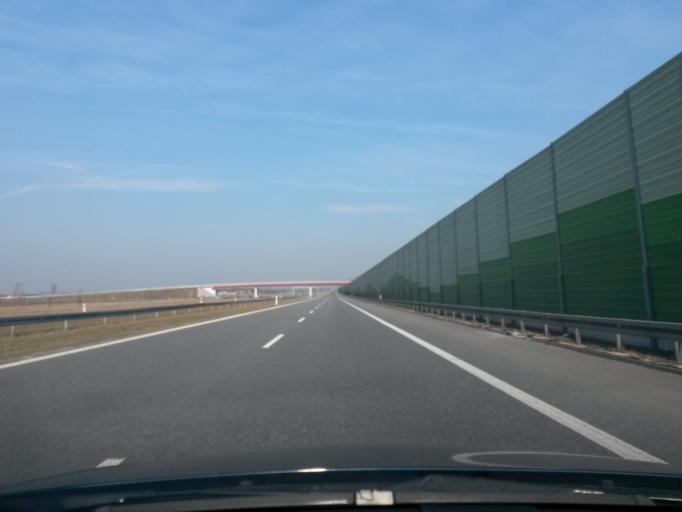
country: PL
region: Lodz Voivodeship
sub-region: Powiat leczycki
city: Piatek
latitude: 52.0814
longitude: 19.5289
